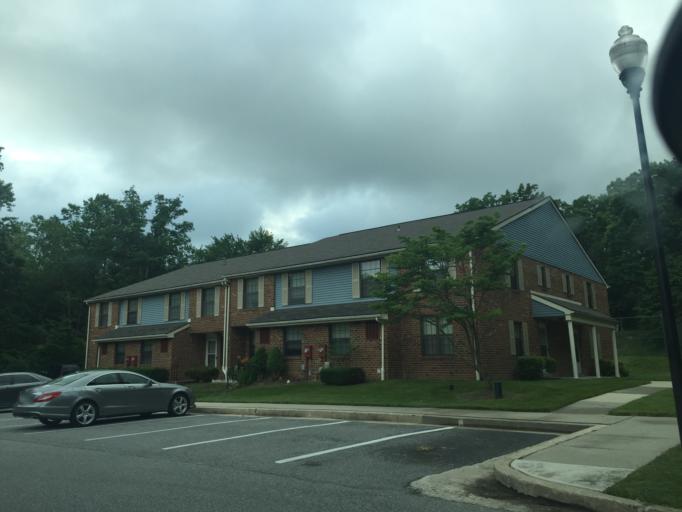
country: US
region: Maryland
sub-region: Baltimore County
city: Carney
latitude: 39.4005
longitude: -76.4928
